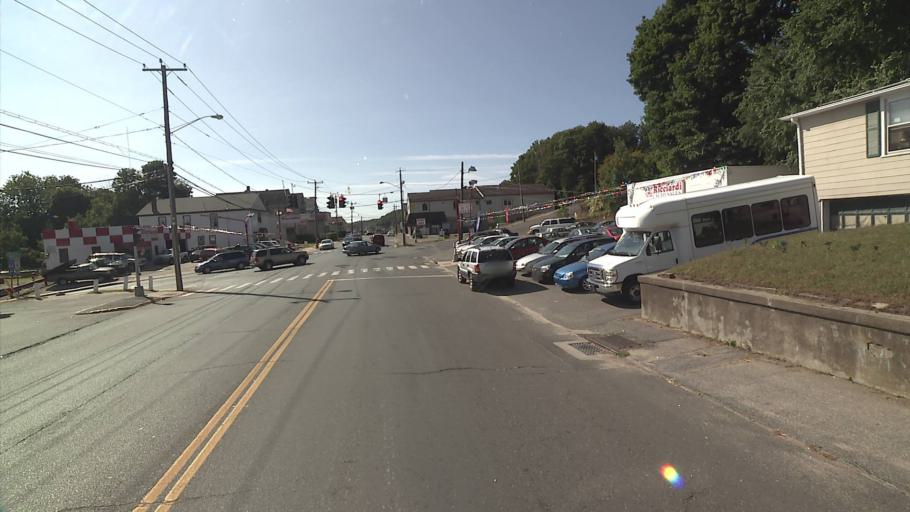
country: US
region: Connecticut
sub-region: New Haven County
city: Waterbury
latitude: 41.5706
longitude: -73.0616
